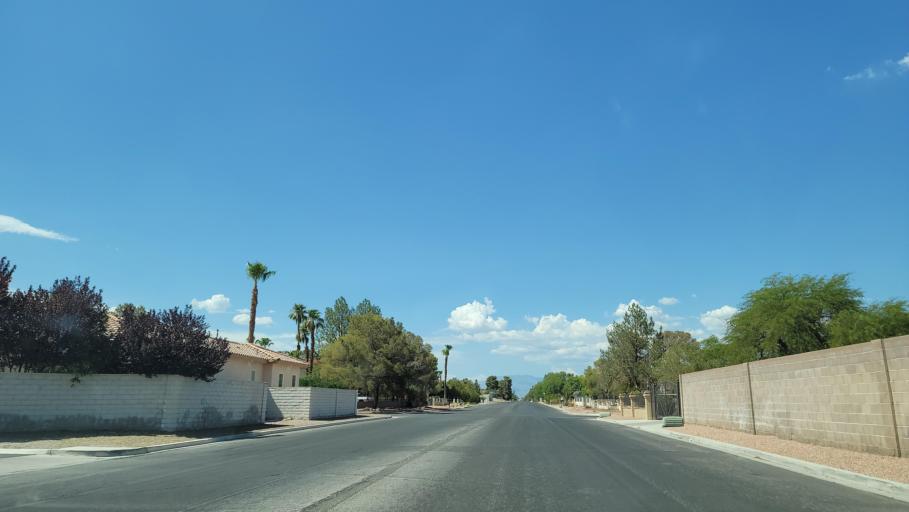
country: US
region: Nevada
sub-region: Clark County
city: Spring Valley
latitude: 36.1305
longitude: -115.2520
